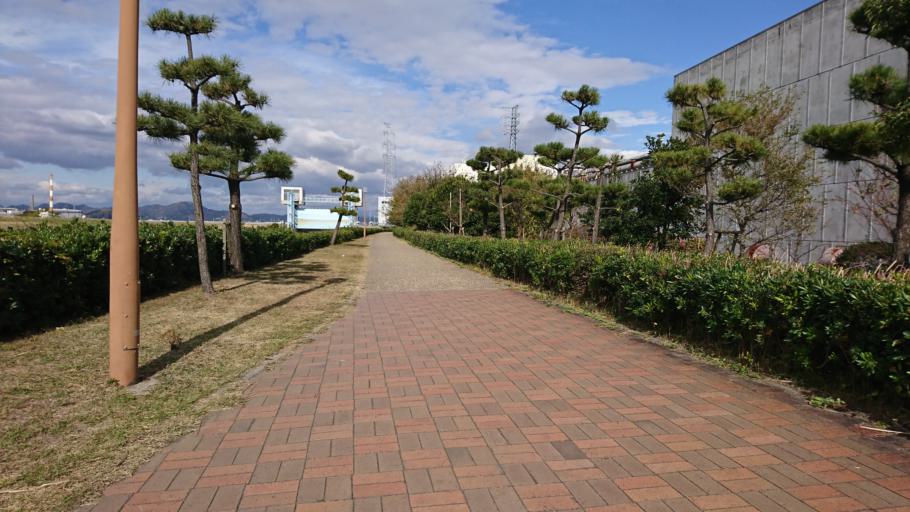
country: JP
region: Hyogo
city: Kakogawacho-honmachi
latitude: 34.7392
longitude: 134.8123
